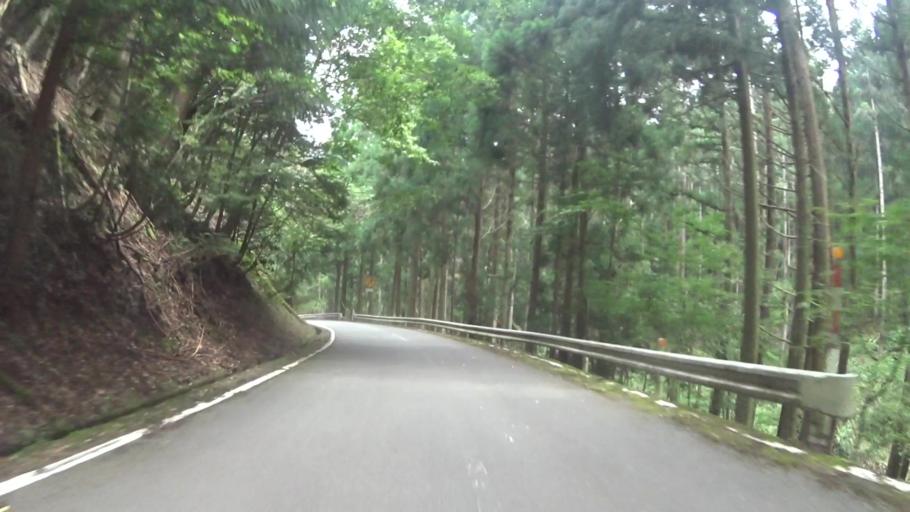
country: JP
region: Kyoto
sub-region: Kyoto-shi
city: Kamigyo-ku
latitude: 35.2020
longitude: 135.6772
